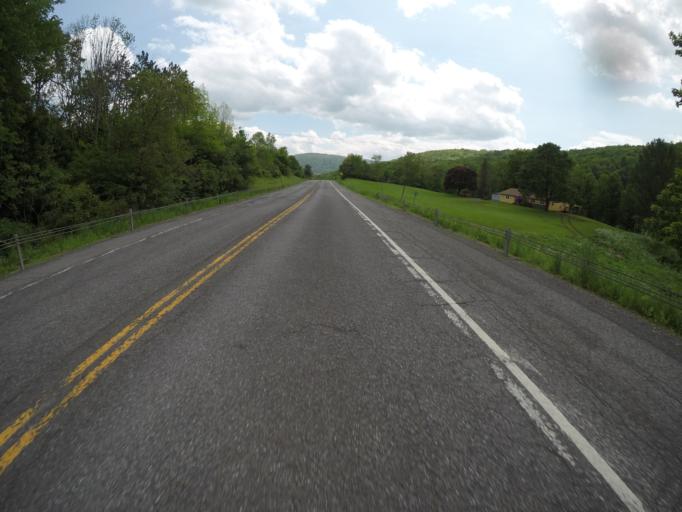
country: US
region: New York
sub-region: Delaware County
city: Stamford
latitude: 42.2056
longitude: -74.5999
